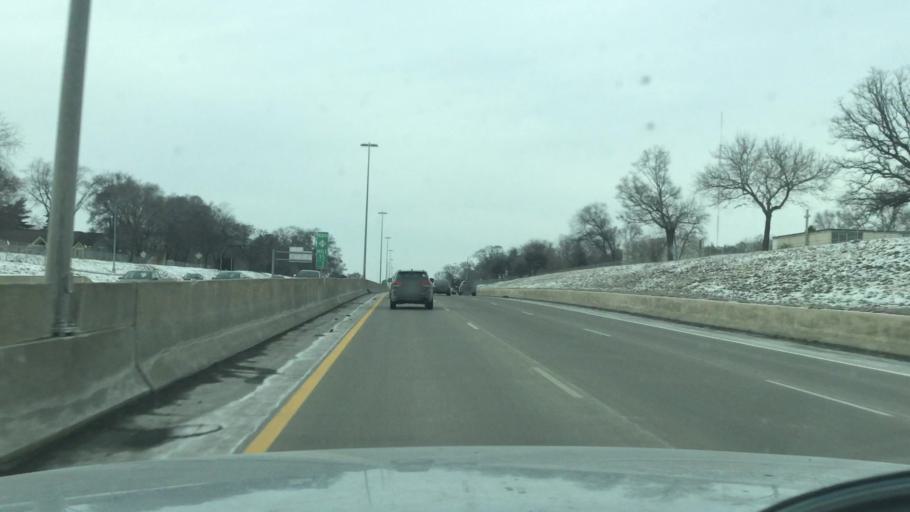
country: US
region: Michigan
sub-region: Oakland County
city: Southfield
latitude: 42.4458
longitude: -83.2197
